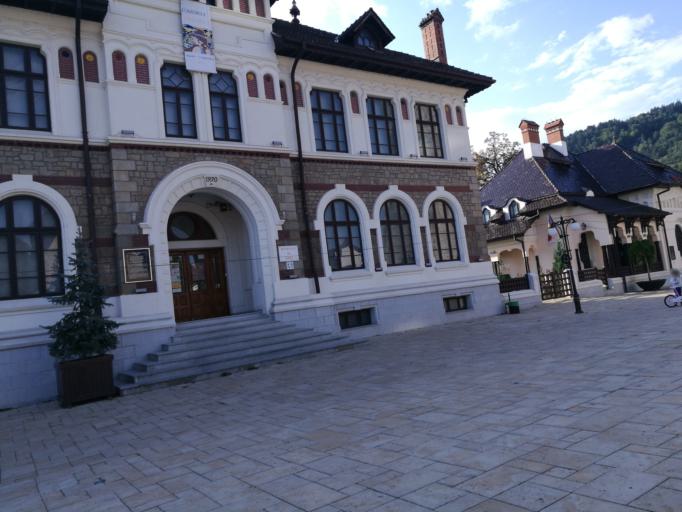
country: RO
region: Neamt
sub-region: Municipiul Piatra-Neamt
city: Valeni
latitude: 46.9329
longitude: 26.3683
